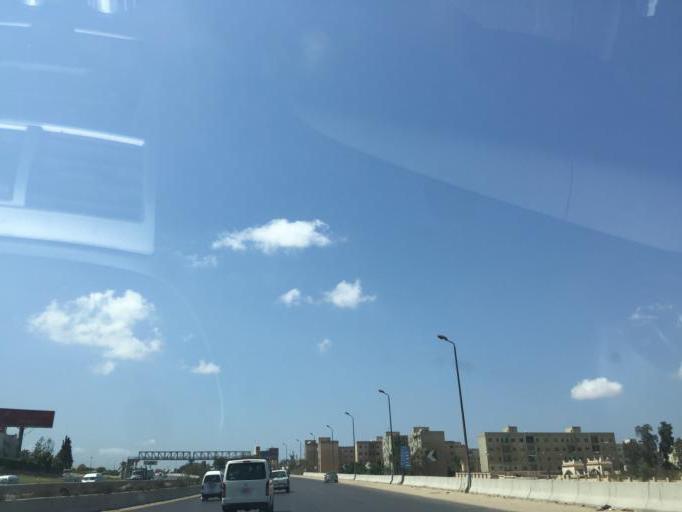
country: EG
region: Alexandria
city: Alexandria
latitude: 31.0235
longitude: 29.7931
